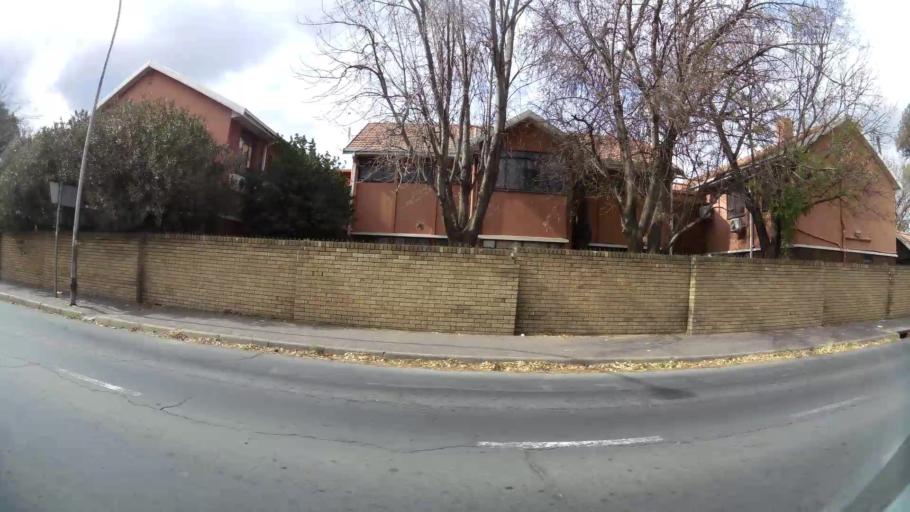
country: ZA
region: Orange Free State
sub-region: Mangaung Metropolitan Municipality
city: Bloemfontein
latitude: -29.1203
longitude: 26.2125
